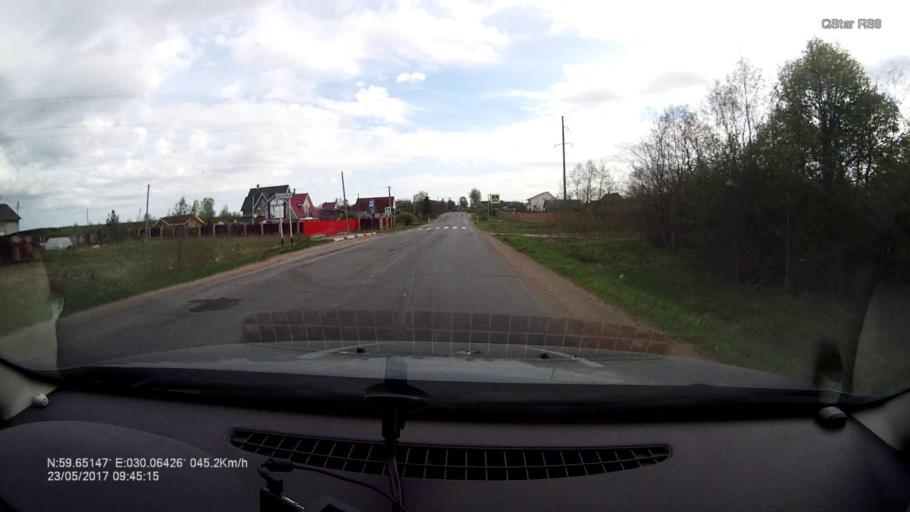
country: RU
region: Leningrad
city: Taytsy
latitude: 59.6515
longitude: 30.0644
